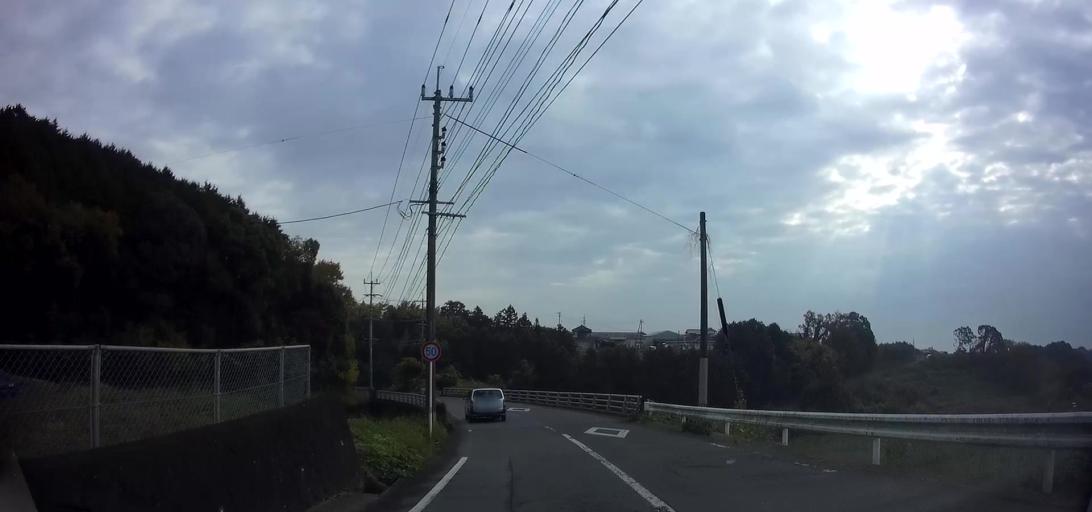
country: JP
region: Nagasaki
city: Shimabara
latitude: 32.6862
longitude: 130.2901
